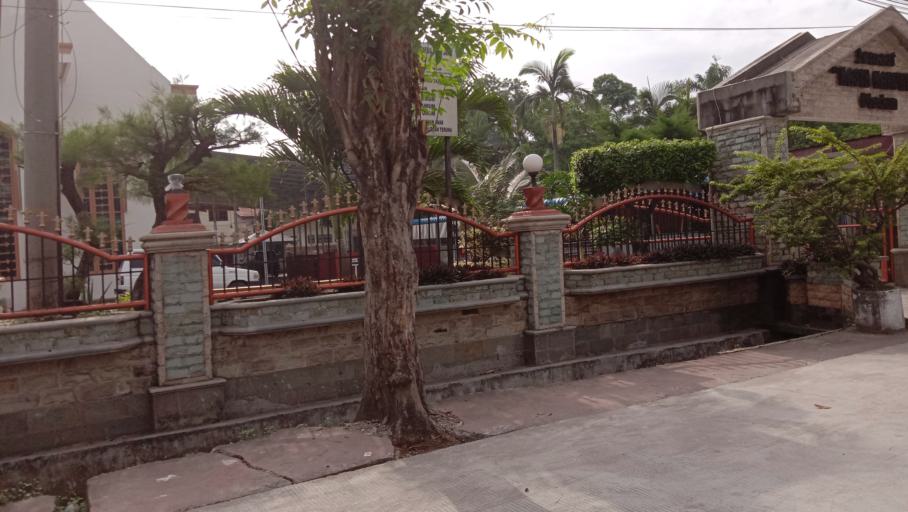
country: ID
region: North Sumatra
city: Medan
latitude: 3.5990
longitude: 98.6450
